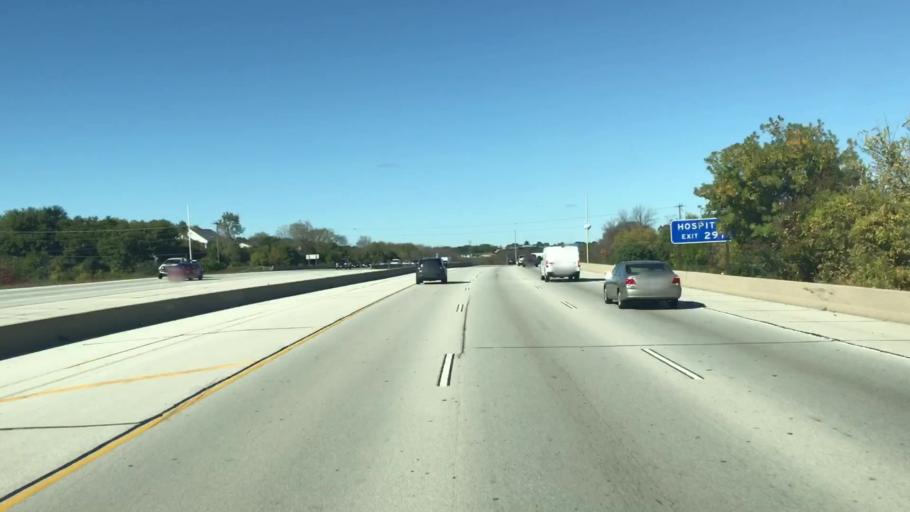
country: US
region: Wisconsin
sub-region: Waukesha County
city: Brookfield
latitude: 43.0295
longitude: -88.1453
